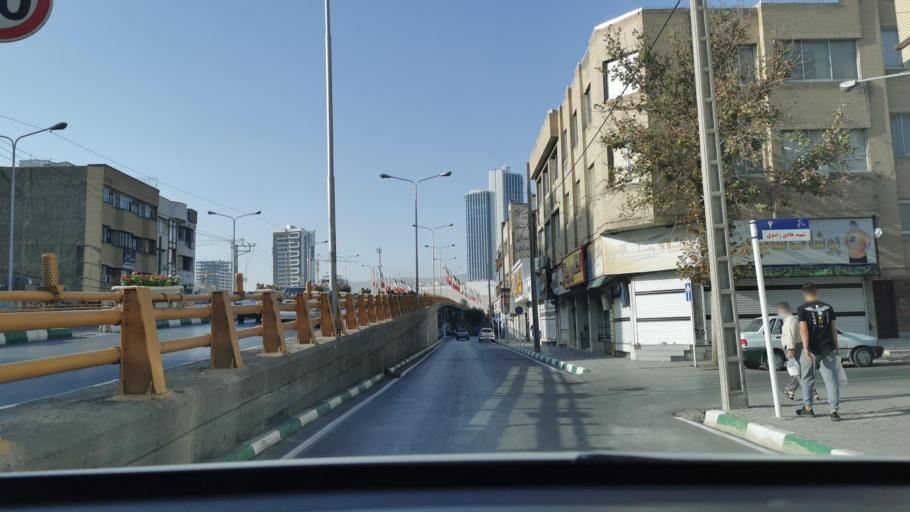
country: IR
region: Razavi Khorasan
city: Mashhad
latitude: 36.3292
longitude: 59.5022
